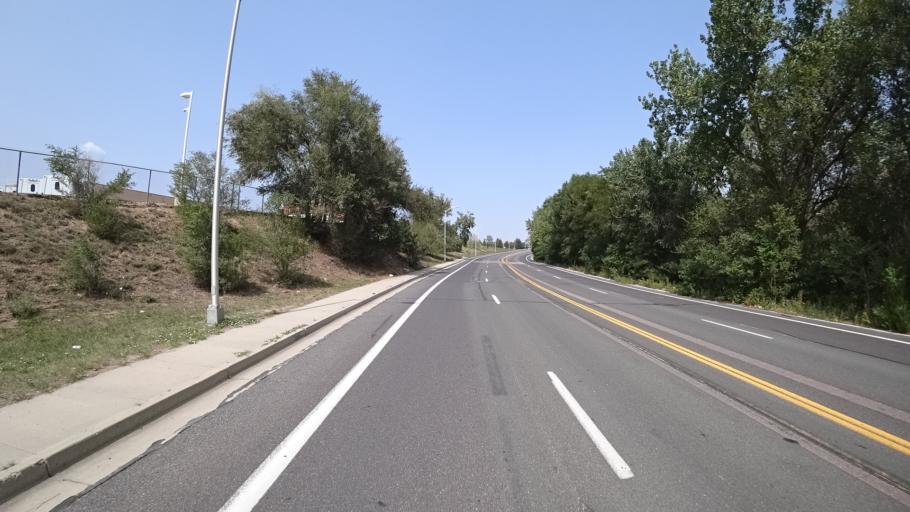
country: US
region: Colorado
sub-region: El Paso County
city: Colorado Springs
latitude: 38.8156
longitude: -104.8045
